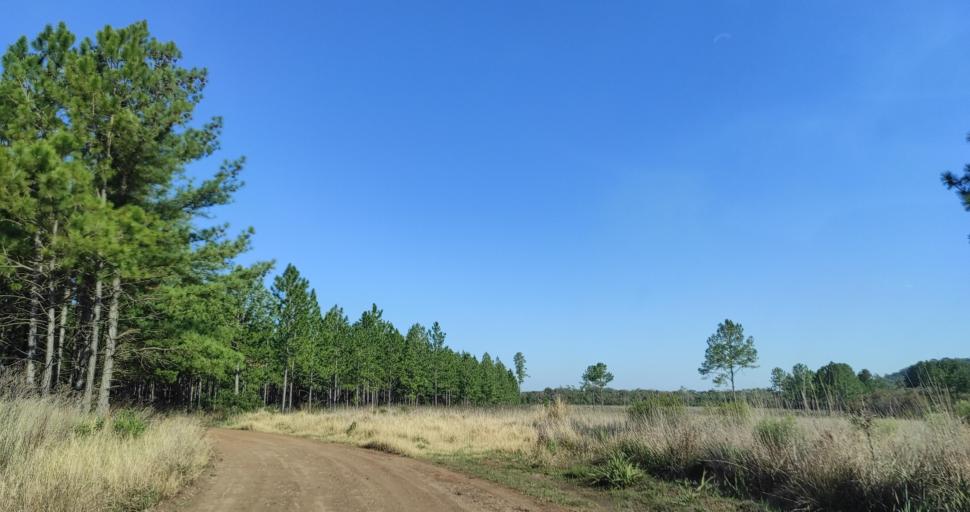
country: AR
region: Misiones
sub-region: Departamento de Apostoles
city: San Jose
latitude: -27.6752
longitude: -55.6596
